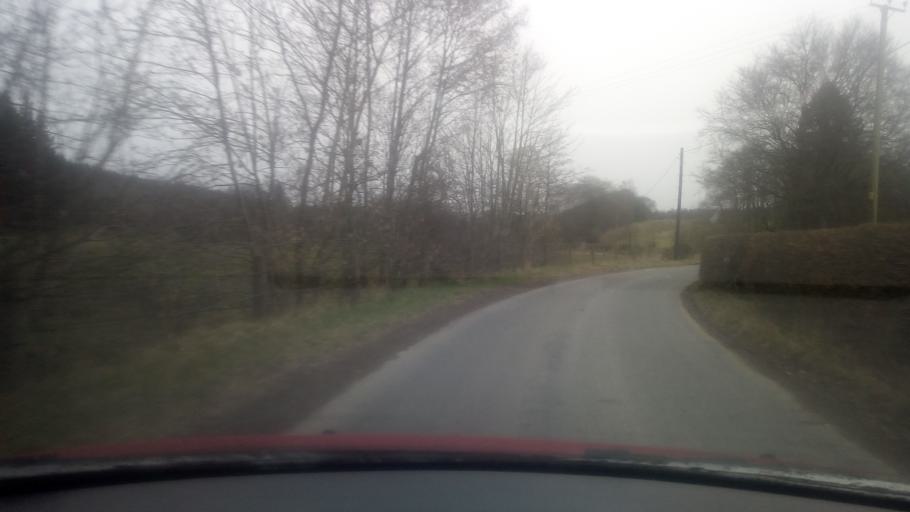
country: GB
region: Scotland
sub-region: The Scottish Borders
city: Jedburgh
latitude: 55.3887
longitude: -2.6535
